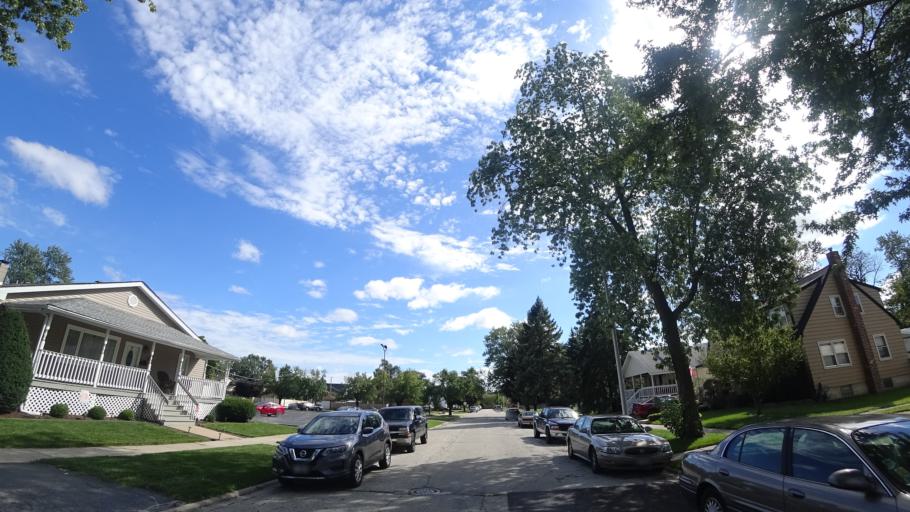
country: US
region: Illinois
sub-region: Cook County
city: Oak Lawn
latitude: 41.7224
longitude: -87.7567
